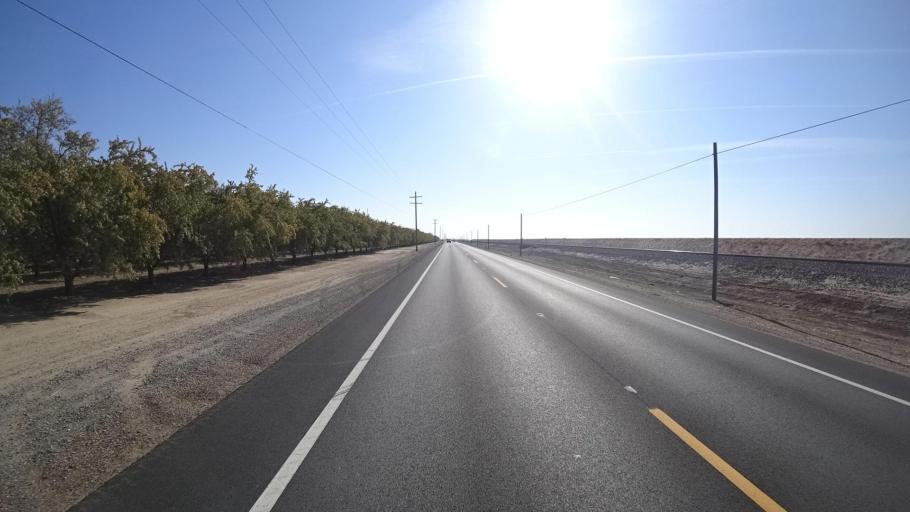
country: US
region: California
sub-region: Kern County
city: Wasco
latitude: 35.6493
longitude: -119.3310
